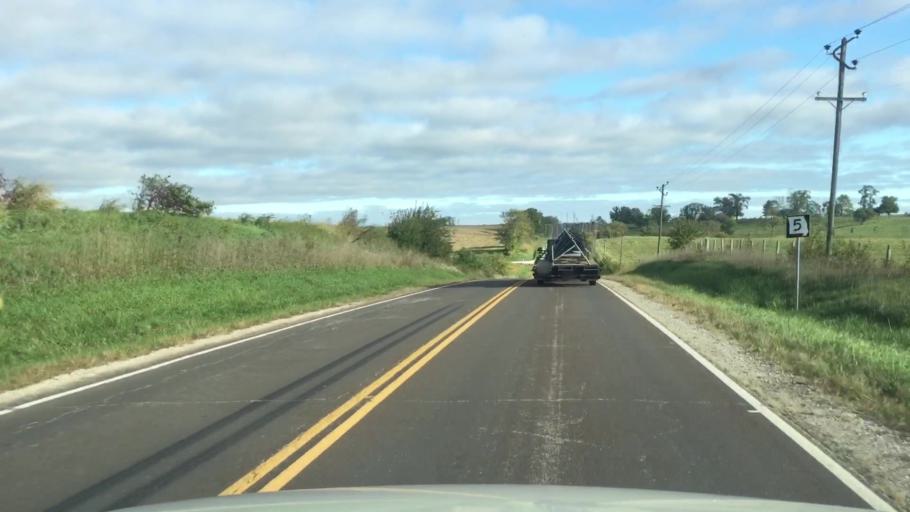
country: US
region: Missouri
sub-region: Howard County
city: New Franklin
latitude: 39.0767
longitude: -92.7457
